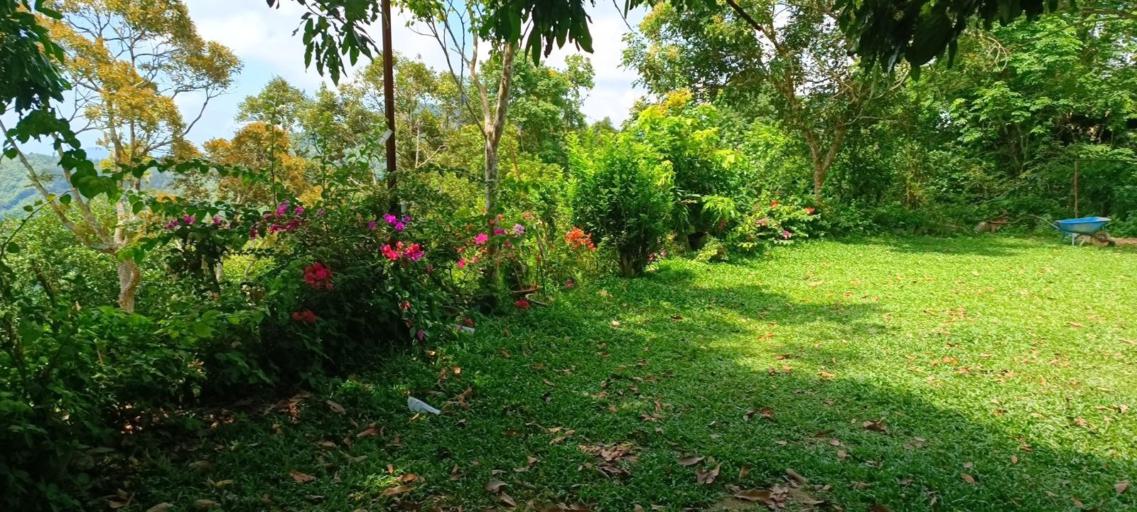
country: MY
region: Penang
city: Kampung Sungai Ara
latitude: 5.3325
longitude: 100.2478
